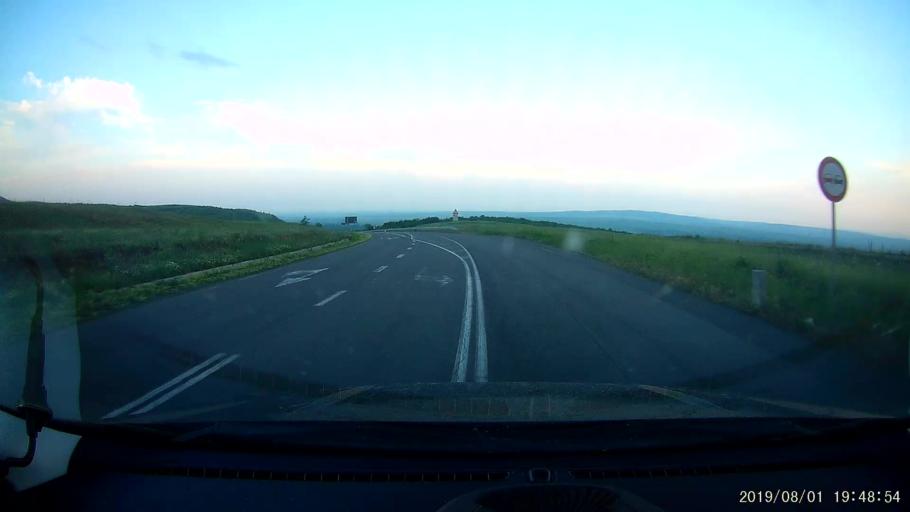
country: BG
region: Burgas
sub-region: Obshtina Karnobat
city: Karnobat
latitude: 42.6301
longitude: 26.9426
